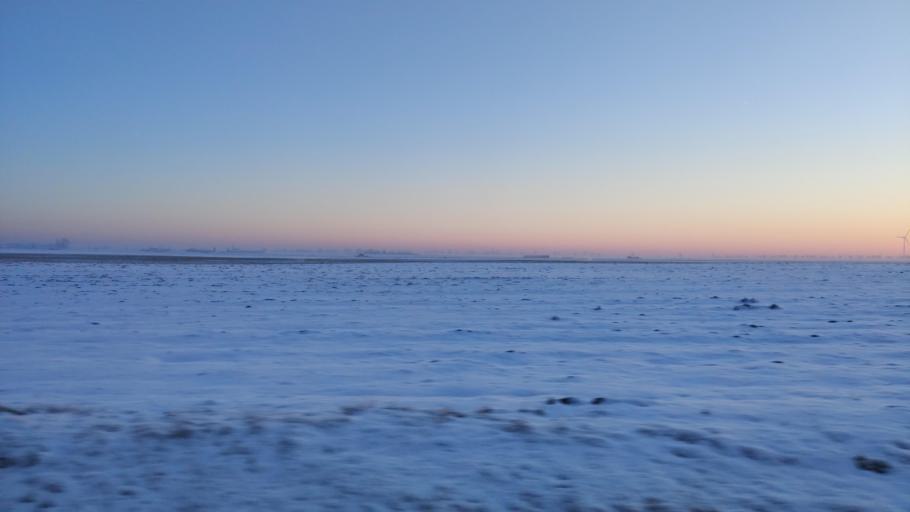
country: PL
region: Kujawsko-Pomorskie
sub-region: Powiat zninski
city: Znin
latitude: 52.8692
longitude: 17.8119
